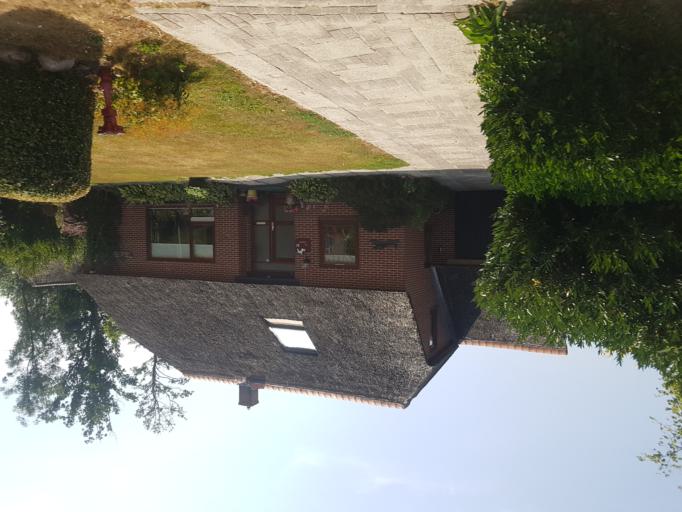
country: NL
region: Overijssel
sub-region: Gemeente Steenwijkerland
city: Giethoorn
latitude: 52.7454
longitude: 6.0791
